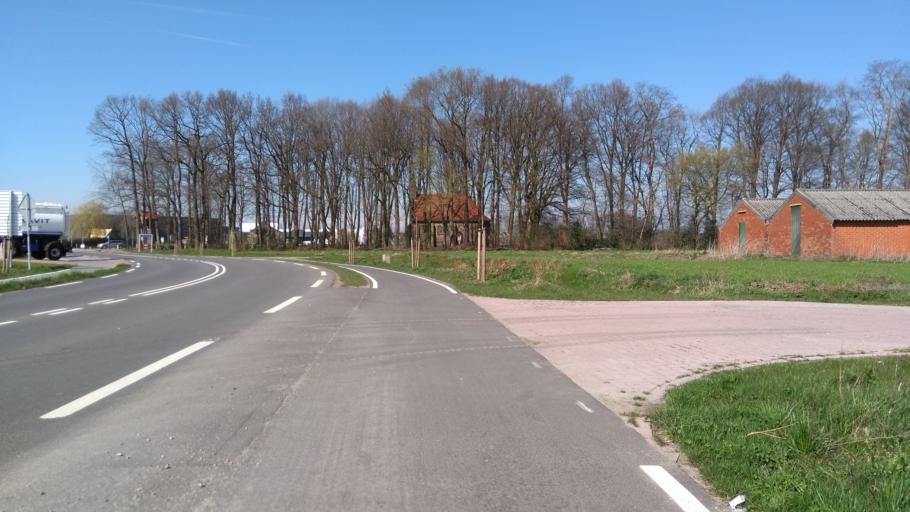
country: NL
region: North Brabant
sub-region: Gemeente Baarle-Nassau
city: Baarle-Nassau
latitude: 51.4406
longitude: 4.9460
